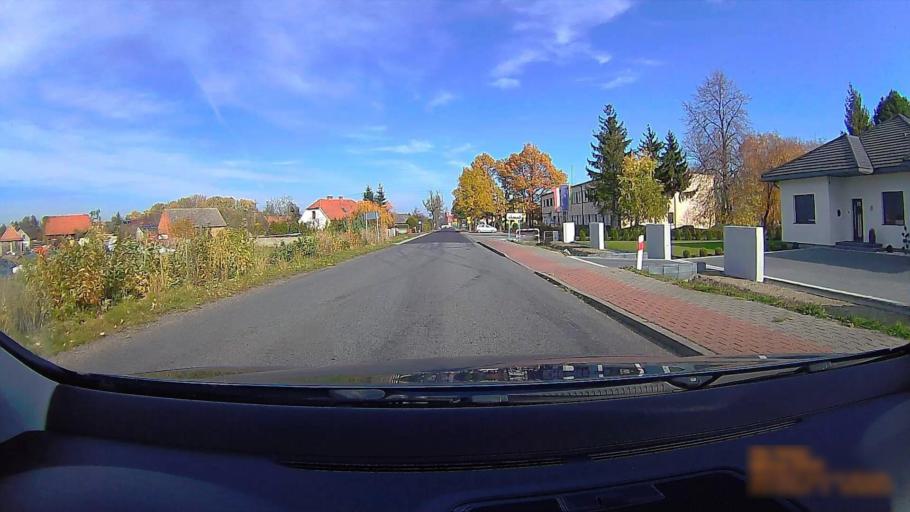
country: PL
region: Greater Poland Voivodeship
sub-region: Powiat ostrzeszowski
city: Doruchow
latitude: 51.4099
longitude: 18.0742
